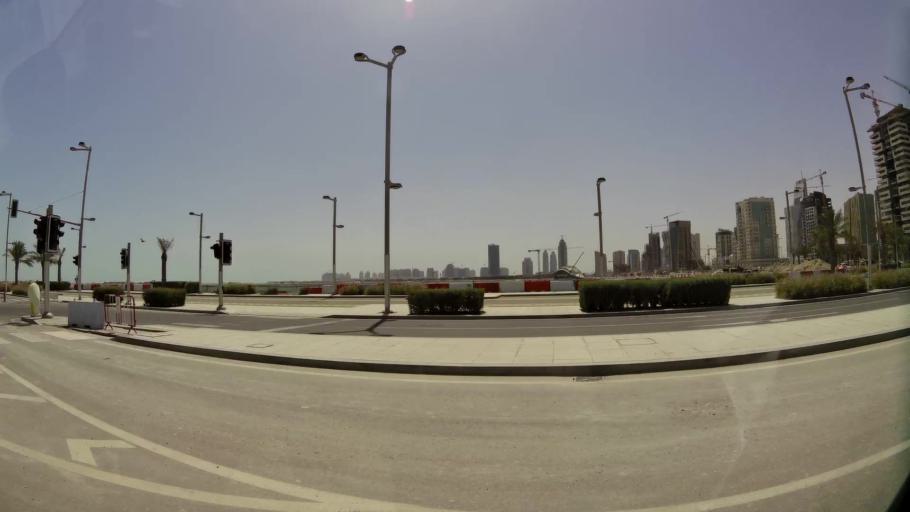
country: QA
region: Baladiyat Umm Salal
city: Umm Salal Muhammad
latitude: 25.4009
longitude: 51.5225
